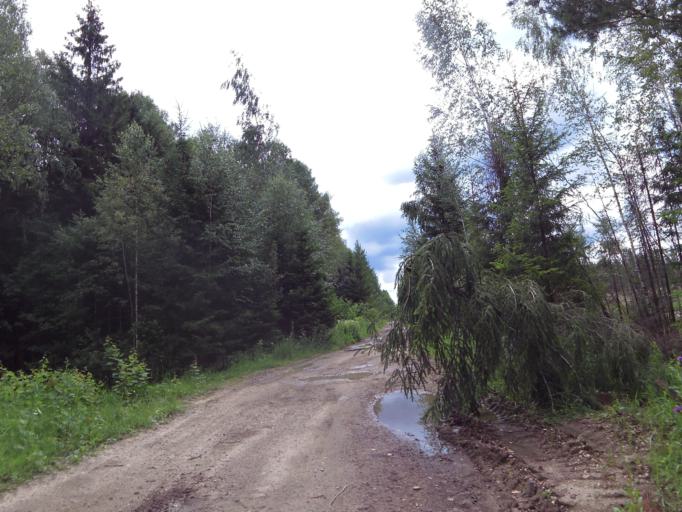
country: RU
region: Moskovskaya
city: Danki
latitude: 54.9390
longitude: 37.6852
